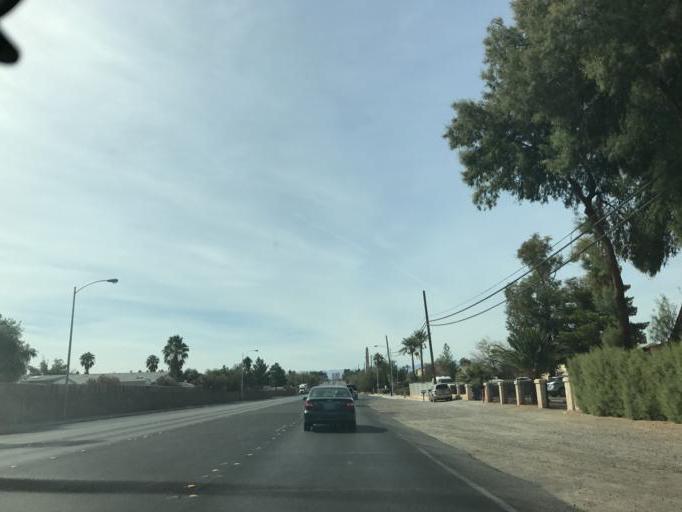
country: US
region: Nevada
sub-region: Clark County
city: Winchester
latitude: 36.1296
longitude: -115.0676
